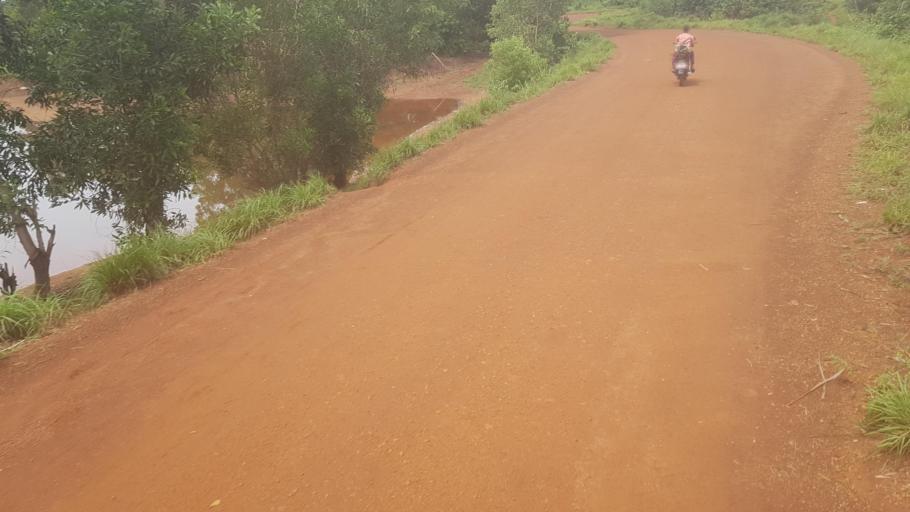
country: SL
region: Southern Province
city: Mogbwemo
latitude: 7.7542
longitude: -12.3077
